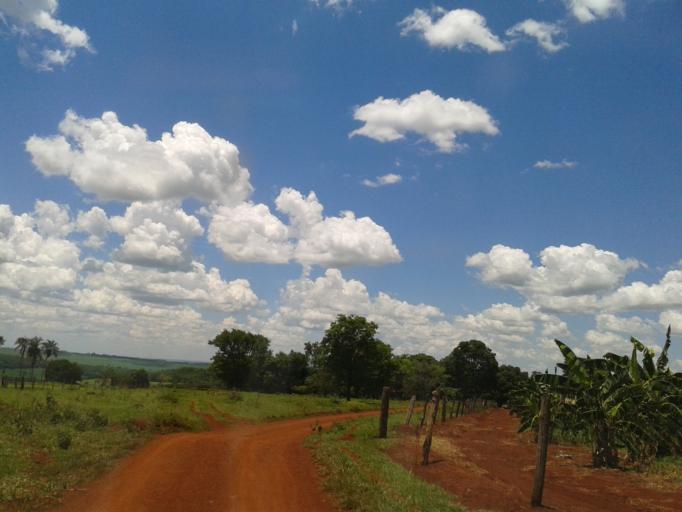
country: BR
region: Minas Gerais
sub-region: Centralina
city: Centralina
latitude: -18.6938
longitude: -49.1953
